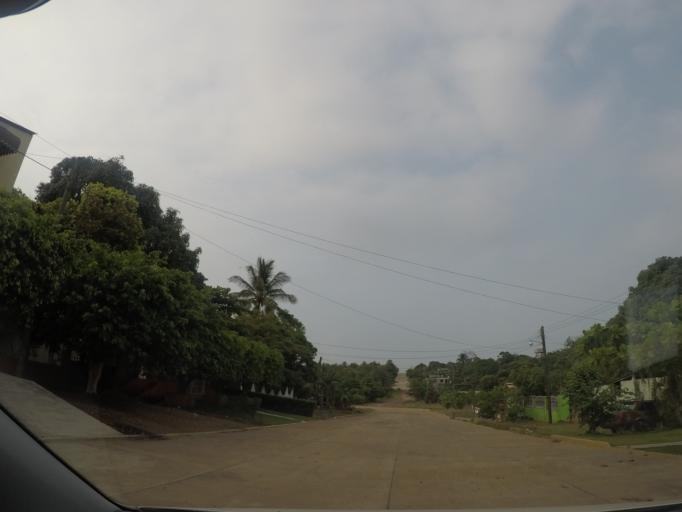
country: MX
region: Oaxaca
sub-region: Santa Maria Petapa
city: Llano Suchiapa
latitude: 16.8687
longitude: -95.0497
